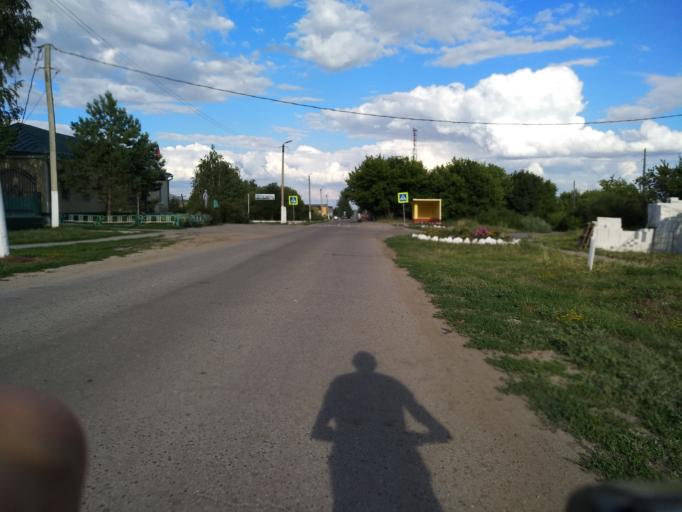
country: RU
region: Lipetsk
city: Dobrinka
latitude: 52.0374
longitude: 40.5503
